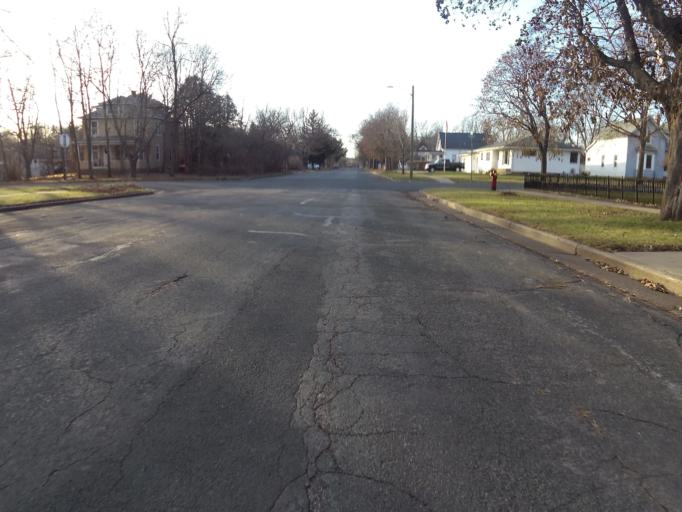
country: US
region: Wisconsin
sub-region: Pierce County
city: River Falls
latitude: 44.8617
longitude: -92.6318
